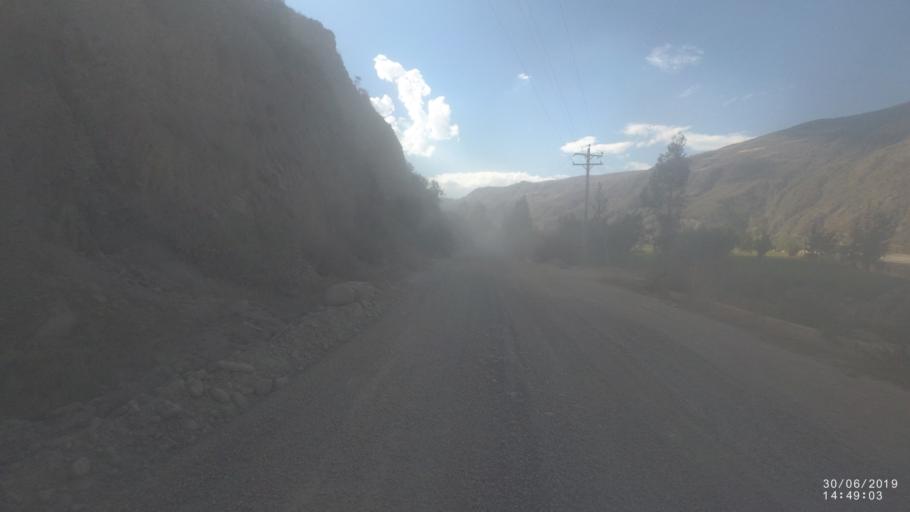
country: BO
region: Cochabamba
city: Irpa Irpa
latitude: -17.7856
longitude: -66.3415
